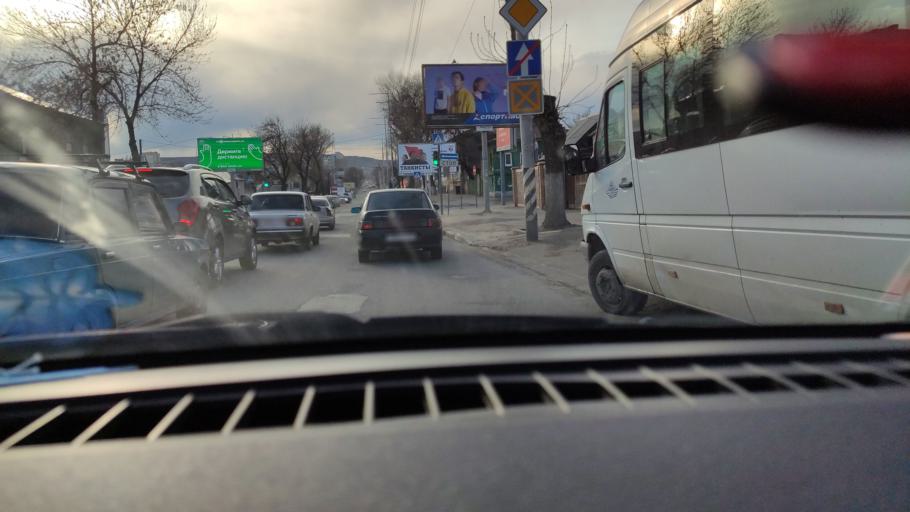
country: RU
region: Saratov
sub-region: Saratovskiy Rayon
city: Saratov
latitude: 51.5440
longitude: 46.0338
